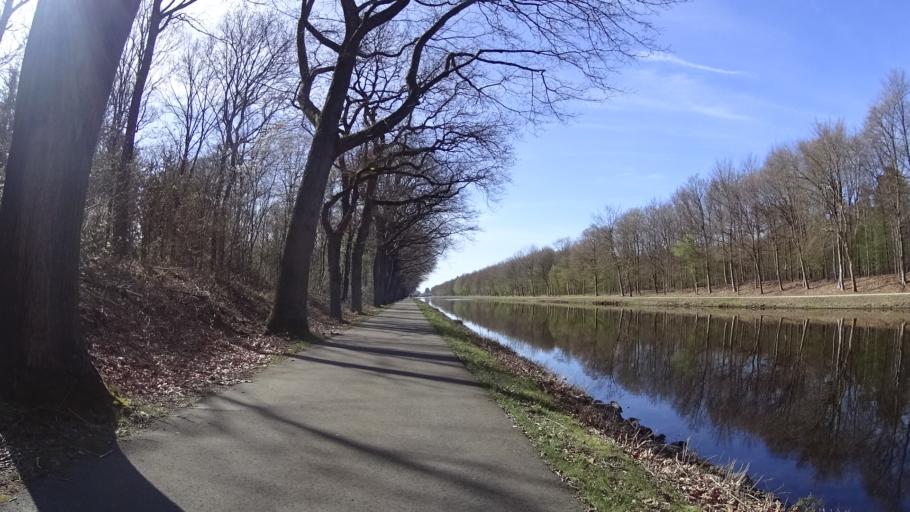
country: DE
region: Lower Saxony
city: Meppen
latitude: 52.6395
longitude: 7.3069
